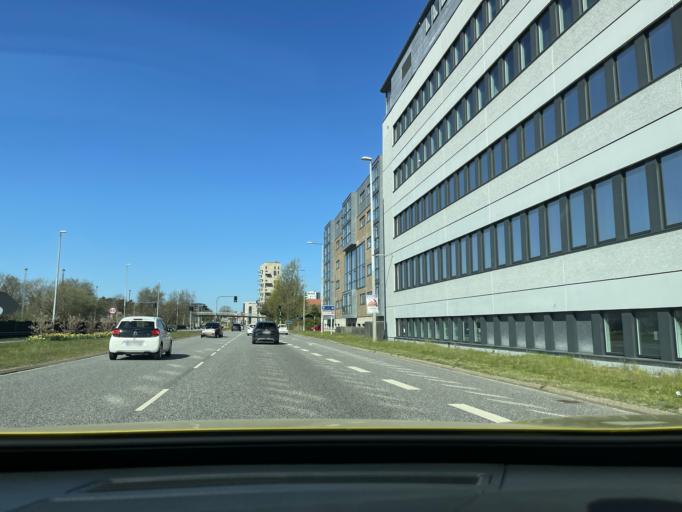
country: DK
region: Central Jutland
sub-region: Herning Kommune
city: Herning
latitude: 56.1332
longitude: 8.9772
